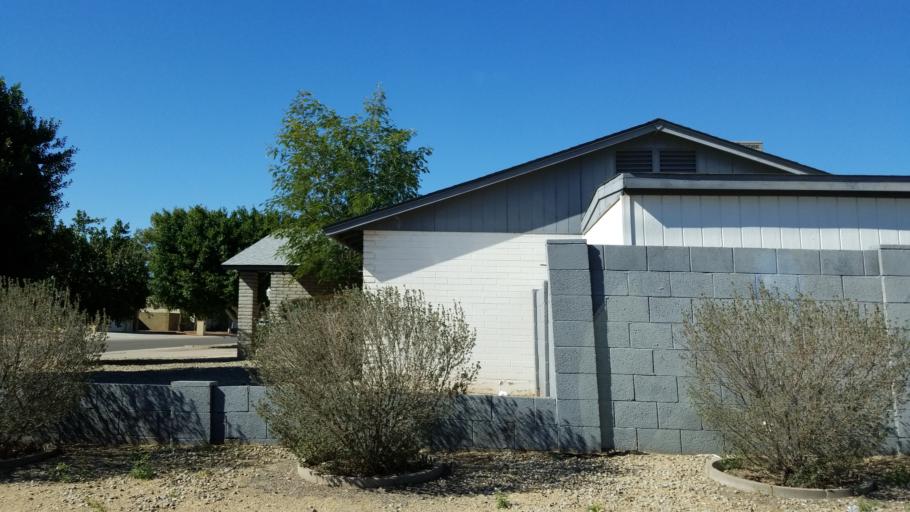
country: US
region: Arizona
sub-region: Maricopa County
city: Glendale
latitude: 33.6527
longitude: -112.1172
